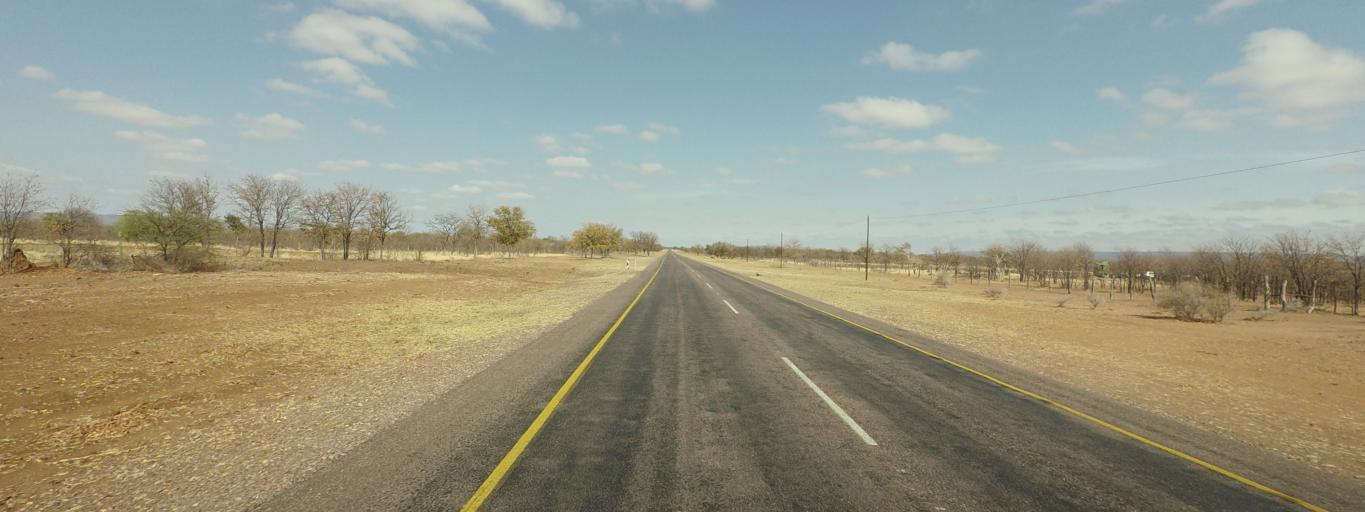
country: BW
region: Central
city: Ramokgonami
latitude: -22.7895
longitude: 27.4458
